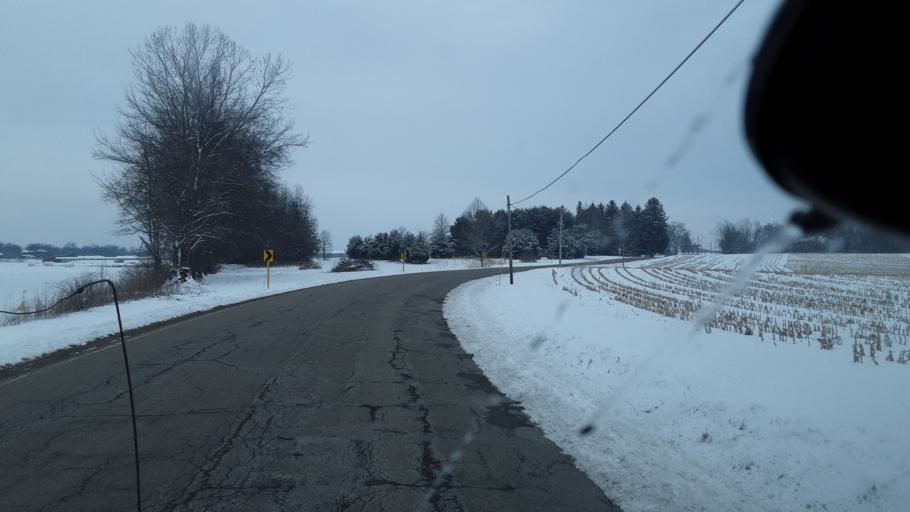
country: US
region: Ohio
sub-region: Licking County
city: Hebron
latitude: 39.9662
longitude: -82.4608
